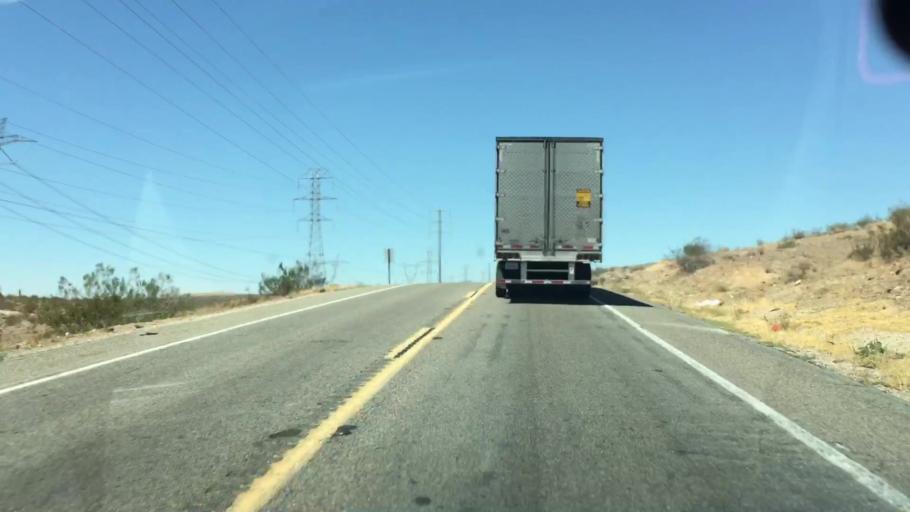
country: US
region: California
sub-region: Kern County
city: Boron
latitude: 34.8675
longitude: -117.5069
